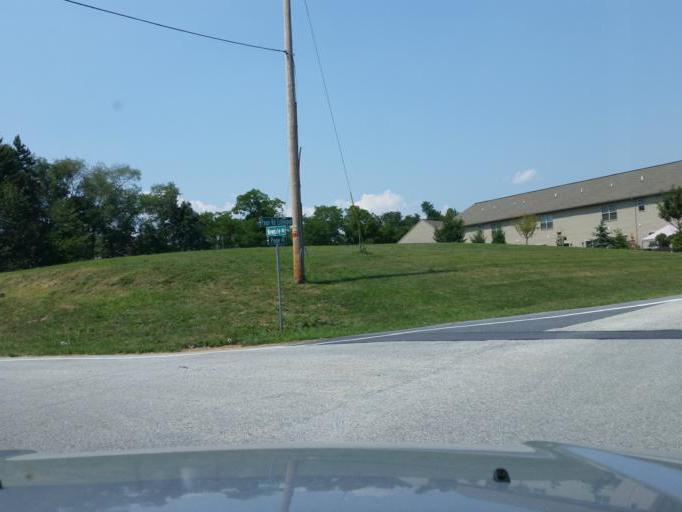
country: US
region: Pennsylvania
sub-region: Dauphin County
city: Rutherford
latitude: 40.2819
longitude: -76.7879
